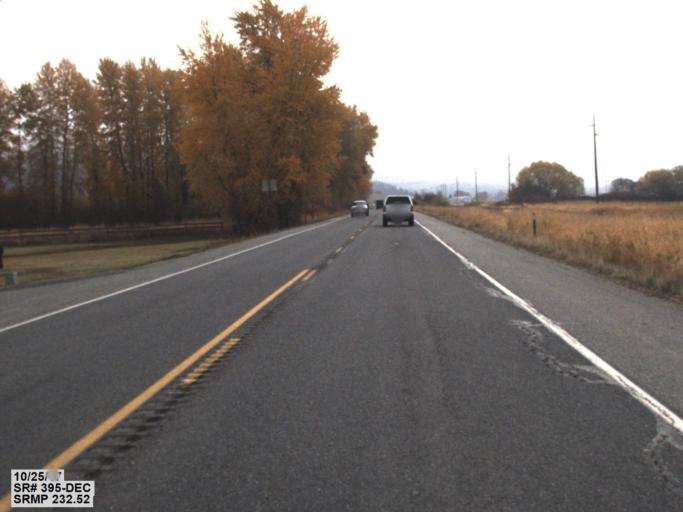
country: US
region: Washington
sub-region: Stevens County
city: Colville
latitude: 48.5750
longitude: -117.9487
